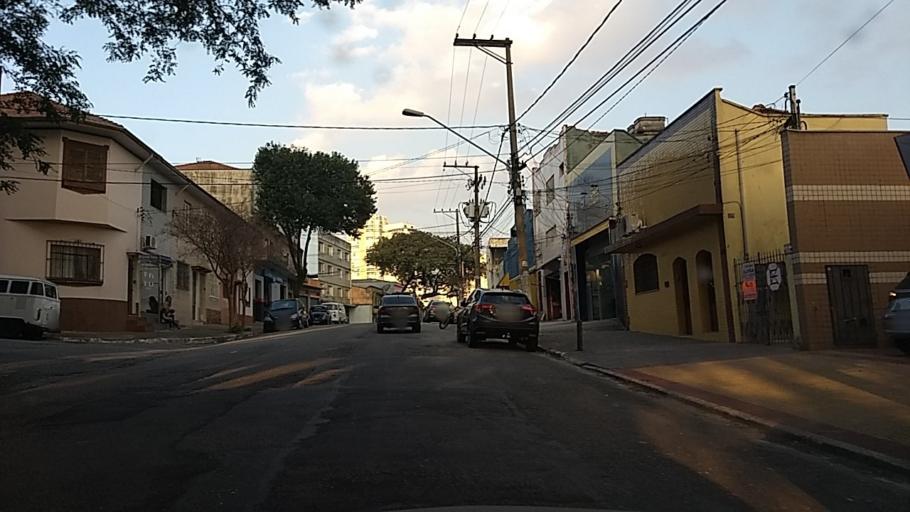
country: BR
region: Sao Paulo
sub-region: Sao Paulo
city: Sao Paulo
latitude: -23.5094
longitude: -46.5908
